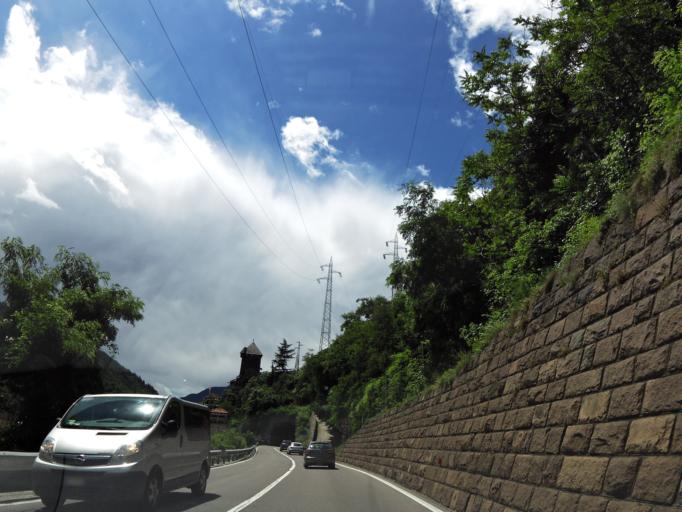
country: IT
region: Trentino-Alto Adige
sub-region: Bolzano
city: Chiusa
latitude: 46.6417
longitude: 11.5675
